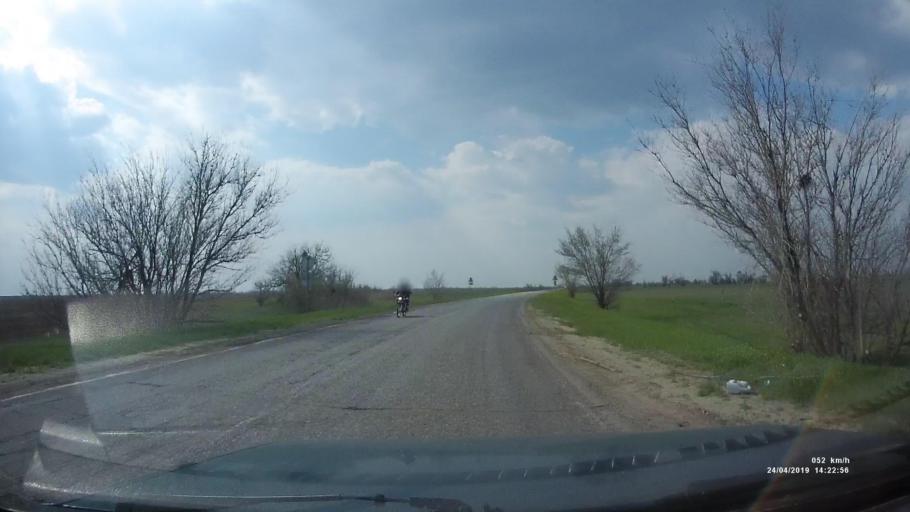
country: RU
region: Kalmykiya
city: Arshan'
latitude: 46.3184
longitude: 44.1203
